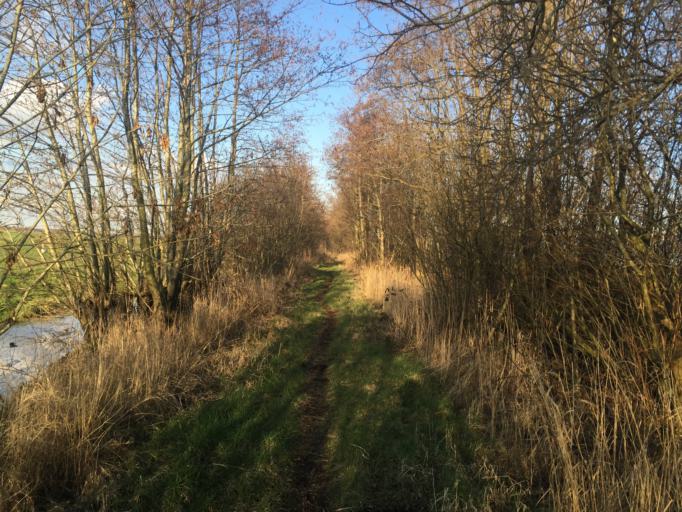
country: NL
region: Utrecht
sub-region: Gemeente Oudewater
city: Oudewater
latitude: 52.0370
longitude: 4.8171
